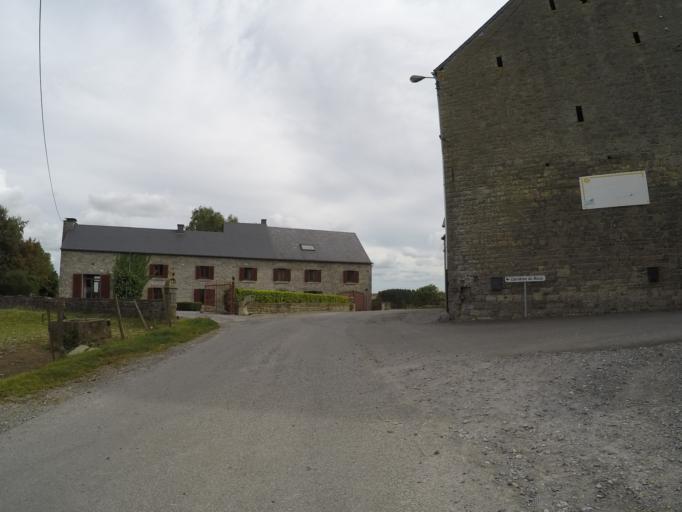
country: BE
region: Wallonia
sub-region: Province de Namur
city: Assesse
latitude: 50.3144
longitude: 4.9782
